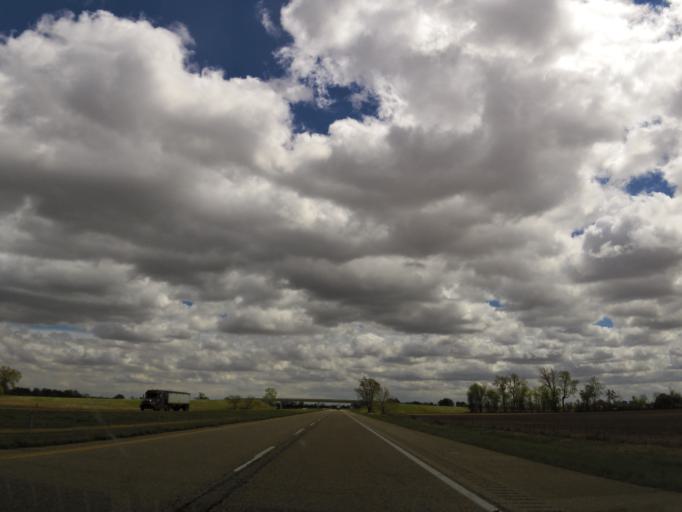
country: US
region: Arkansas
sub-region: Poinsett County
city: Trumann
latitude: 35.6484
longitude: -90.5222
